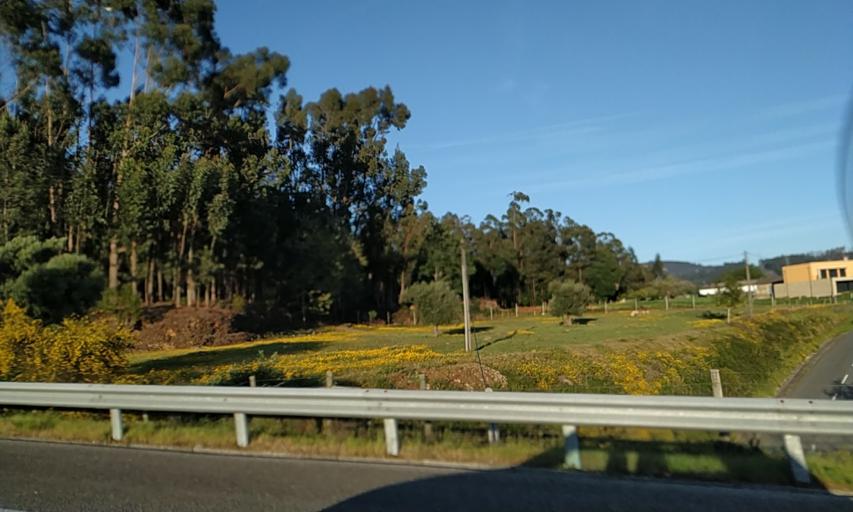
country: PT
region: Viana do Castelo
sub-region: Ponte de Lima
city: Ponte de Lima
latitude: 41.6826
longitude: -8.5393
